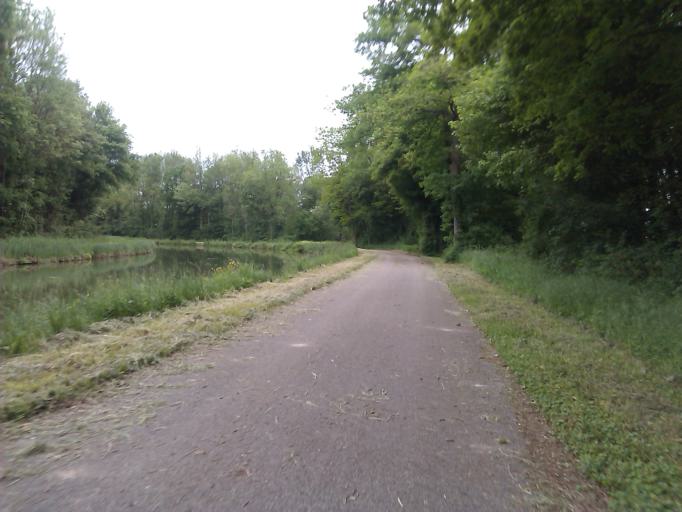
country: FR
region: Franche-Comte
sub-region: Departement du Jura
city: Damparis
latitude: 47.0828
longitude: 5.3584
